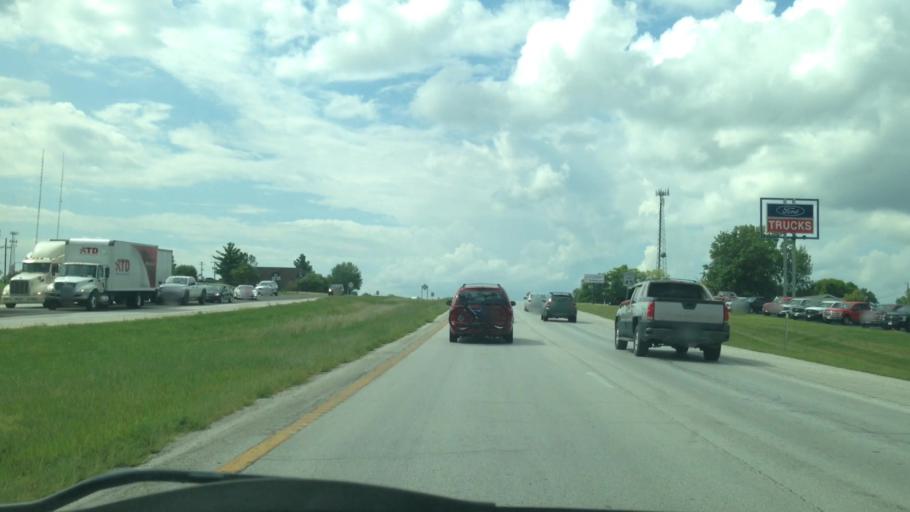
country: US
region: Missouri
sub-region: Marion County
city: Hannibal
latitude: 39.7287
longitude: -91.3949
